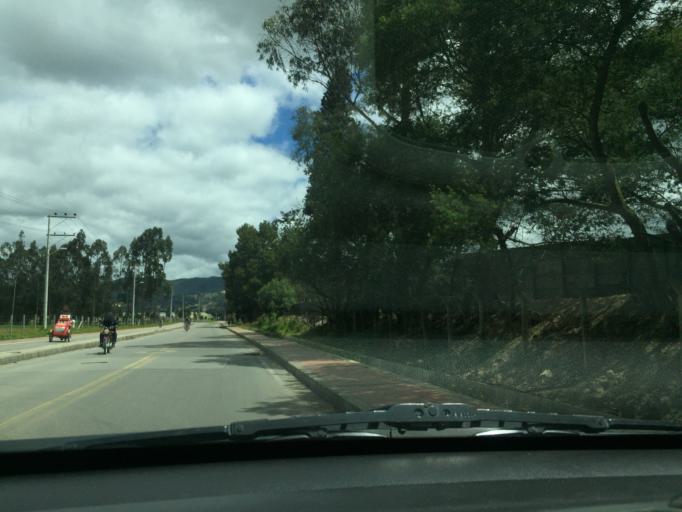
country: CO
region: Cundinamarca
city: Tocancipa
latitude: 4.9643
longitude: -73.9491
